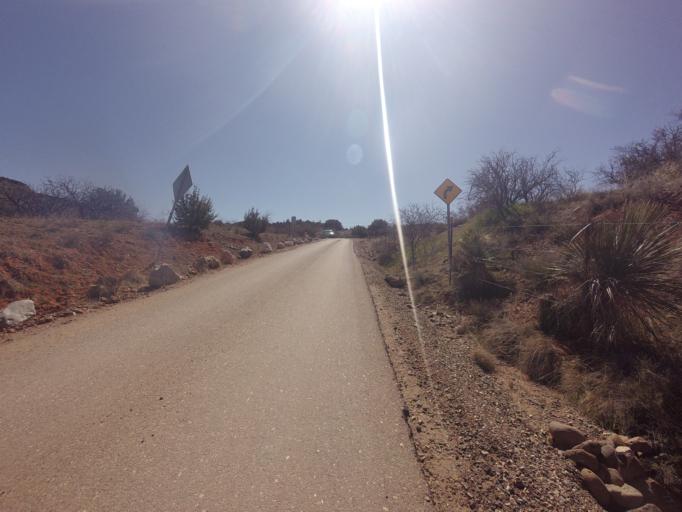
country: US
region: Arizona
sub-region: Yavapai County
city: Lake Montezuma
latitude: 34.6684
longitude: -111.7133
